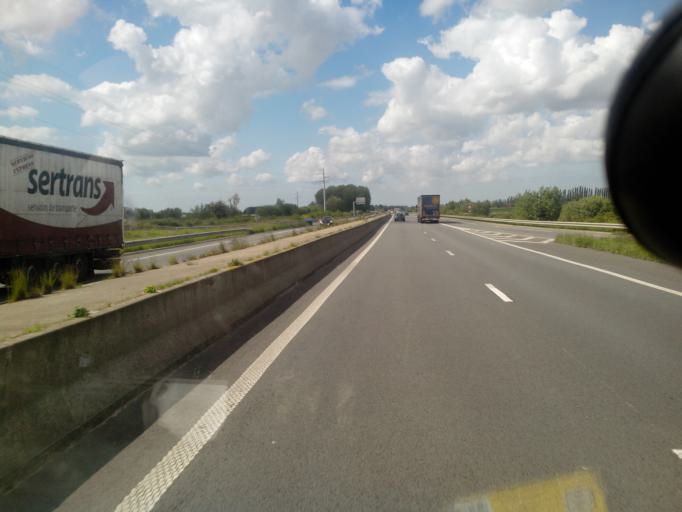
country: FR
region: Nord-Pas-de-Calais
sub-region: Departement du Nord
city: Herzeele
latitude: 50.8865
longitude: 2.5142
